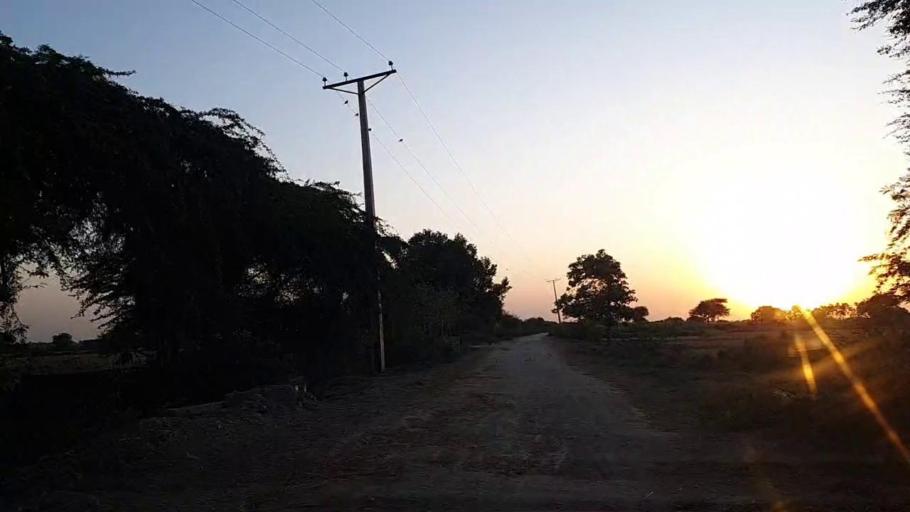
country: PK
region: Sindh
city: Mirpur Batoro
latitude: 24.6333
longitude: 68.1890
